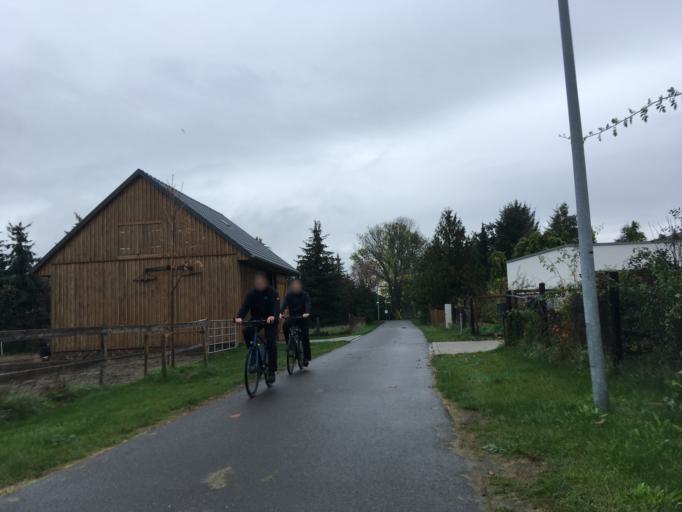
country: DE
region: Brandenburg
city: Friedland
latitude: 52.0388
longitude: 14.1785
